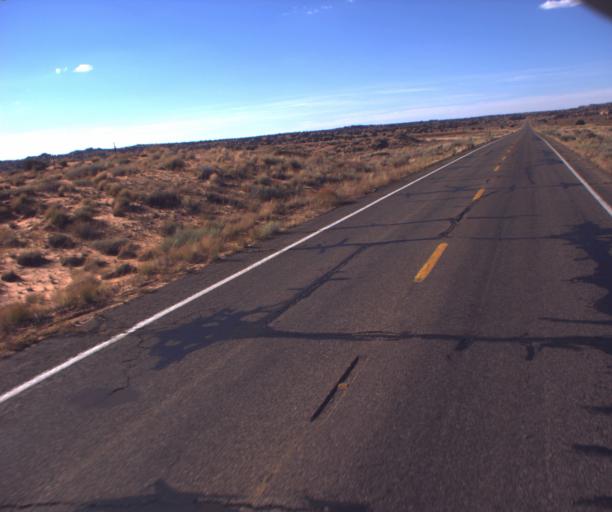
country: US
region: Arizona
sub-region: Coconino County
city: Kaibito
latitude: 36.6061
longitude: -111.1784
